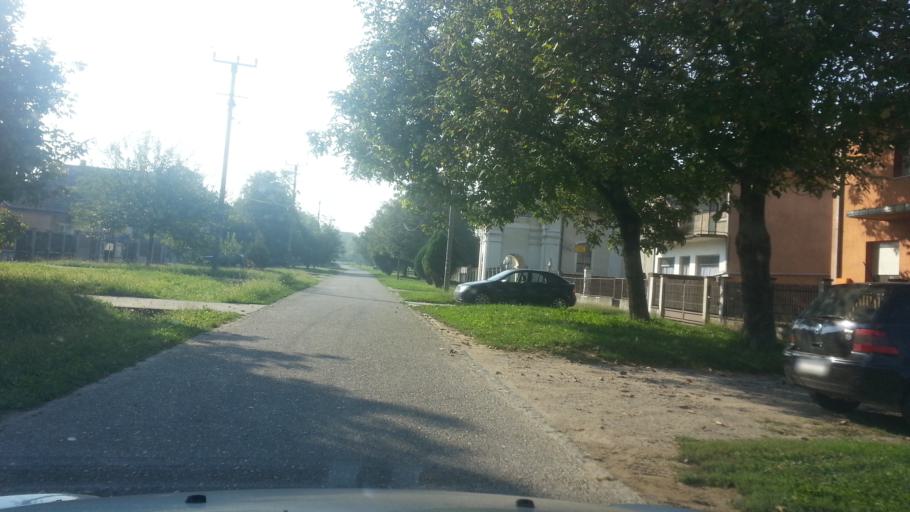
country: RS
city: Novi Banovci
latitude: 44.9554
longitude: 20.2855
